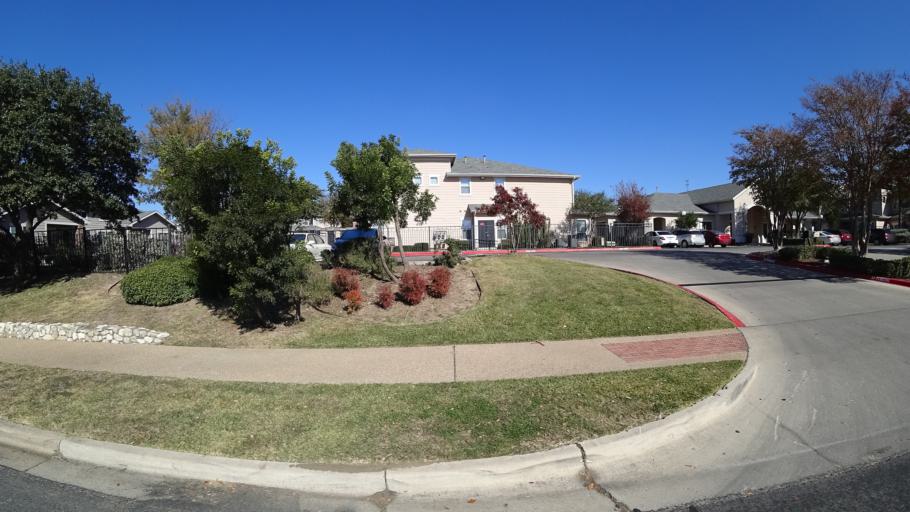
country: US
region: Texas
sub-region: Travis County
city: Wells Branch
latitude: 30.4344
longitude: -97.6951
